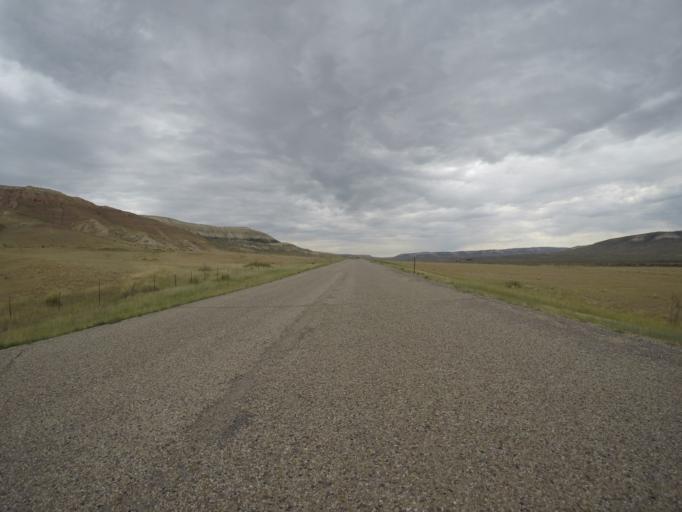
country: US
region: Wyoming
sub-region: Lincoln County
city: Kemmerer
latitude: 41.8230
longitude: -110.7457
